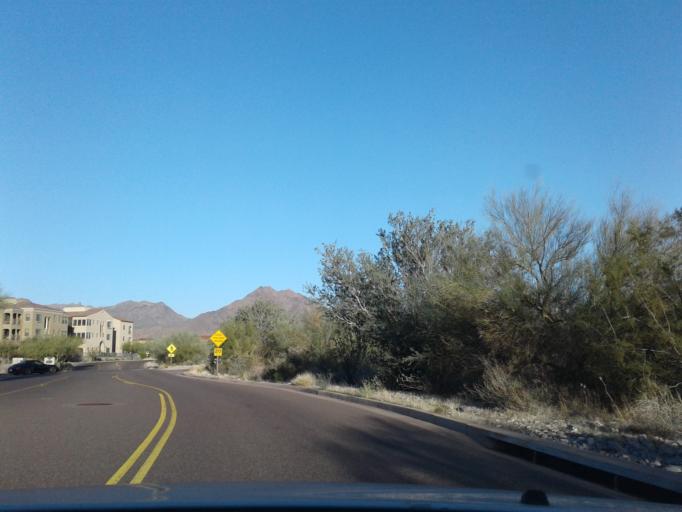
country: US
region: Arizona
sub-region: Maricopa County
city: Paradise Valley
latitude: 33.6498
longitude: -111.8873
